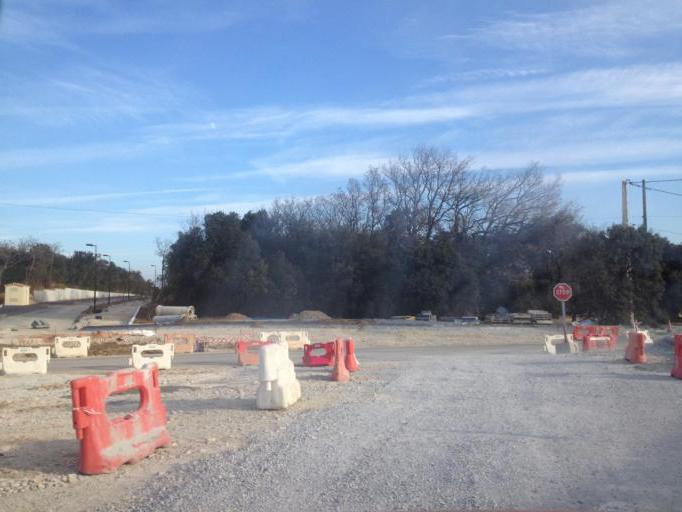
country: FR
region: Provence-Alpes-Cote d'Azur
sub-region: Departement du Vaucluse
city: Orange
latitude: 44.1148
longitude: 4.8198
